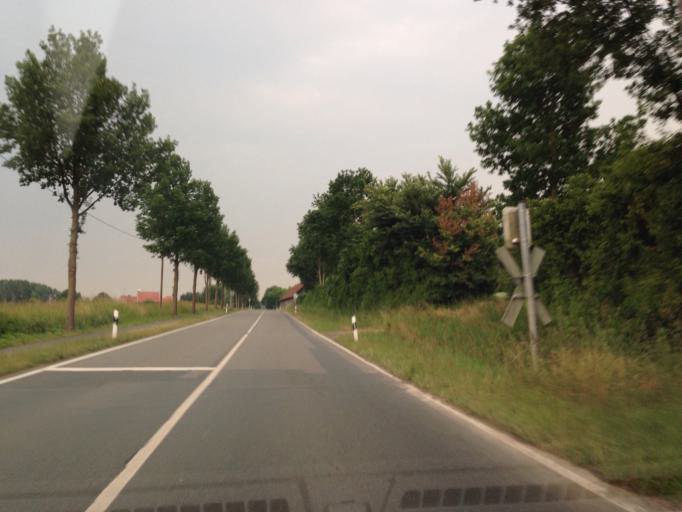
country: DE
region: North Rhine-Westphalia
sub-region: Regierungsbezirk Munster
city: Havixbeck
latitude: 51.9591
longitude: 7.4265
